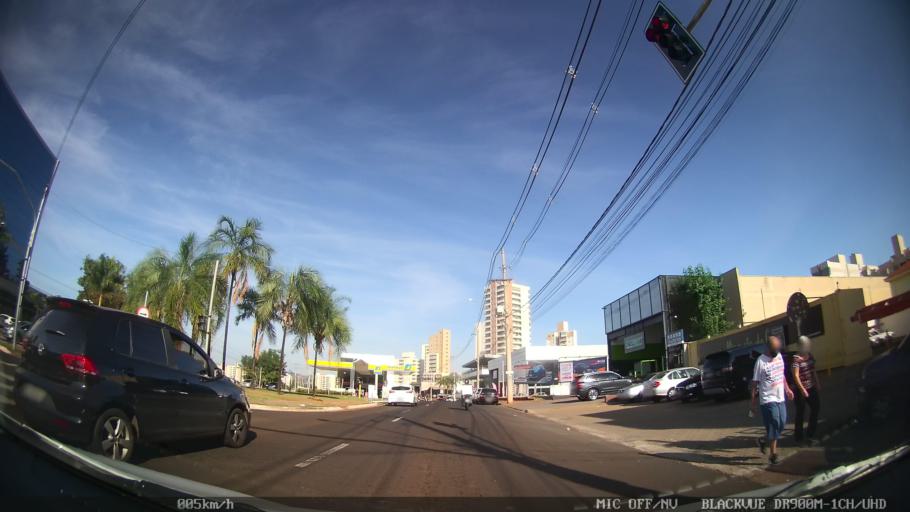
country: BR
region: Sao Paulo
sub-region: Ribeirao Preto
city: Ribeirao Preto
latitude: -21.2168
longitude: -47.8247
